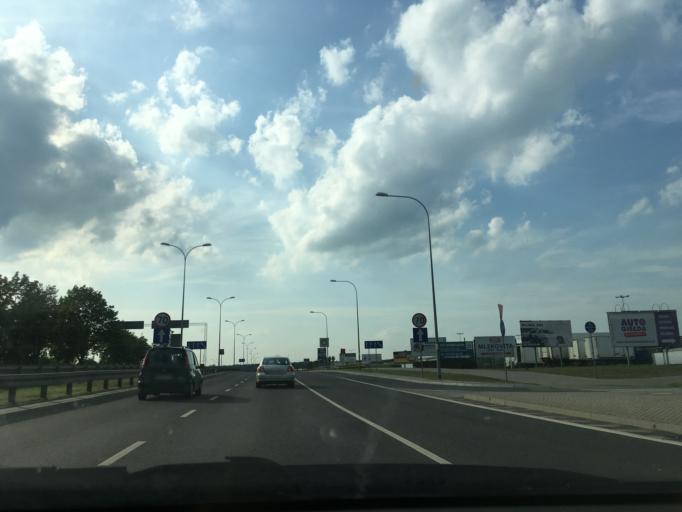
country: PL
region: Podlasie
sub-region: Bialystok
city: Bialystok
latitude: 53.1529
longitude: 23.1649
